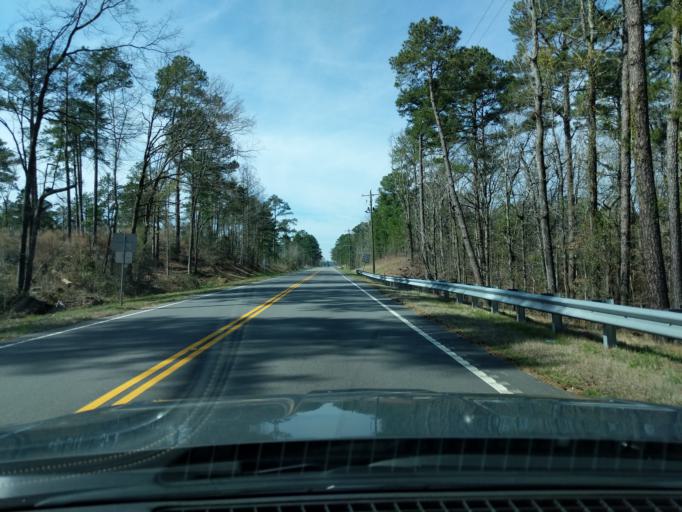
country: US
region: Georgia
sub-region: Columbia County
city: Evans
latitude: 33.6729
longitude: -82.1784
